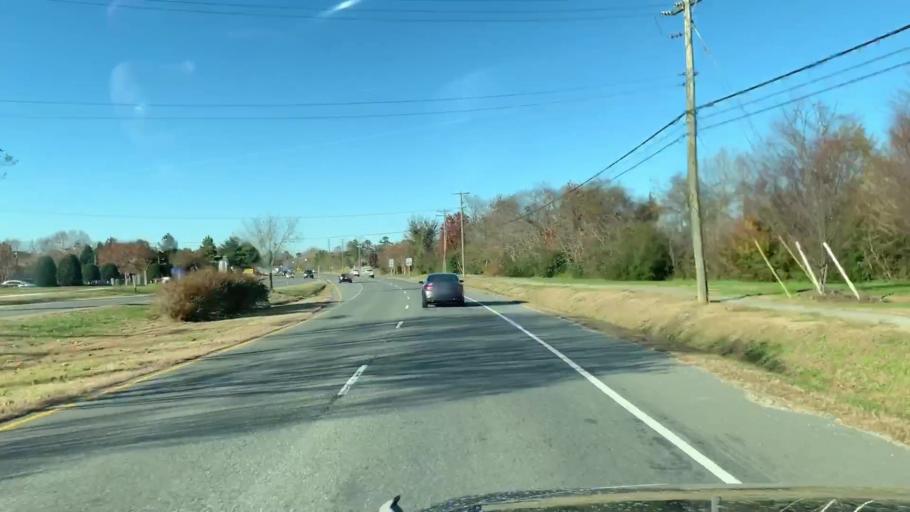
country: US
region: Virginia
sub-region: James City County
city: Williamsburg
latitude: 37.3578
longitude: -76.7643
